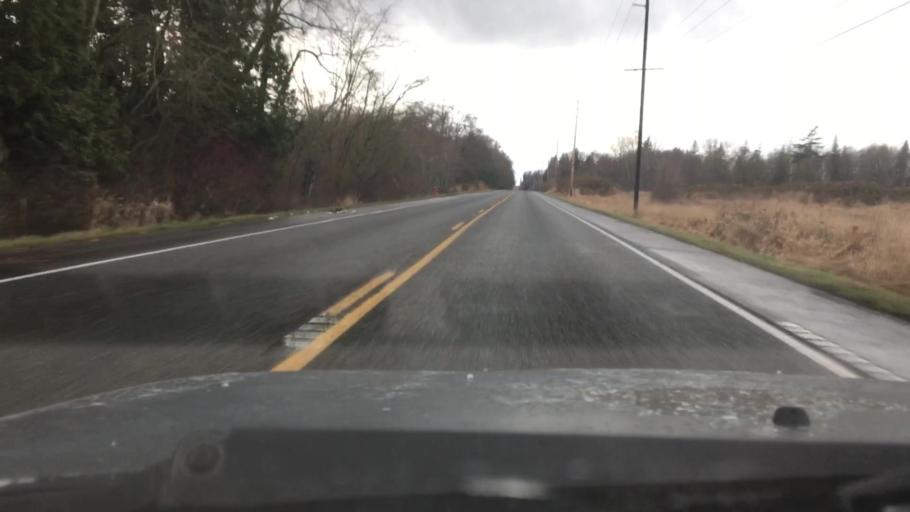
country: US
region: Washington
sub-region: Whatcom County
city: Ferndale
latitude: 48.8194
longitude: -122.6448
